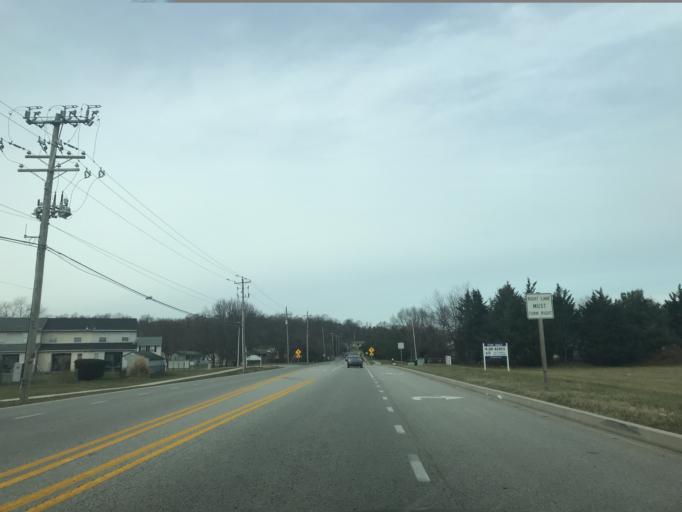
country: US
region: Maryland
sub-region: Cecil County
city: Elkton
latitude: 39.6070
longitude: -75.7901
